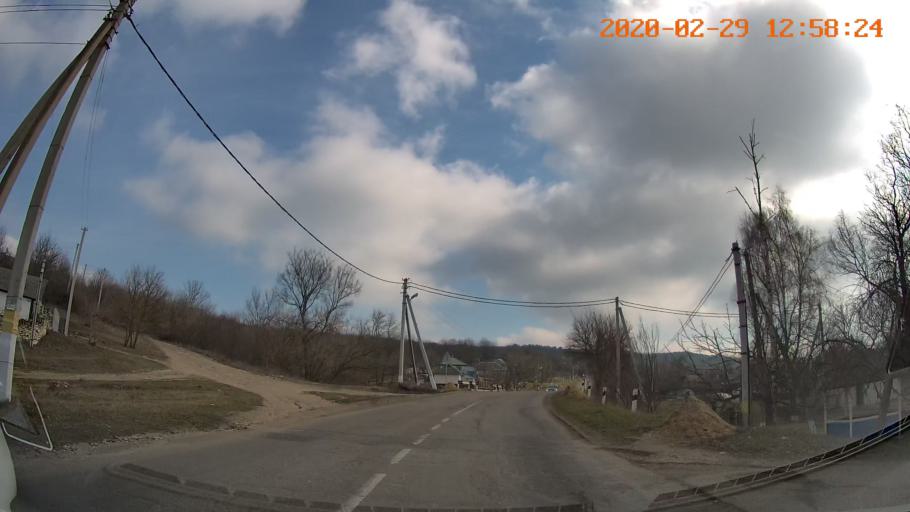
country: MD
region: Telenesti
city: Camenca
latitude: 48.0704
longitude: 28.7206
